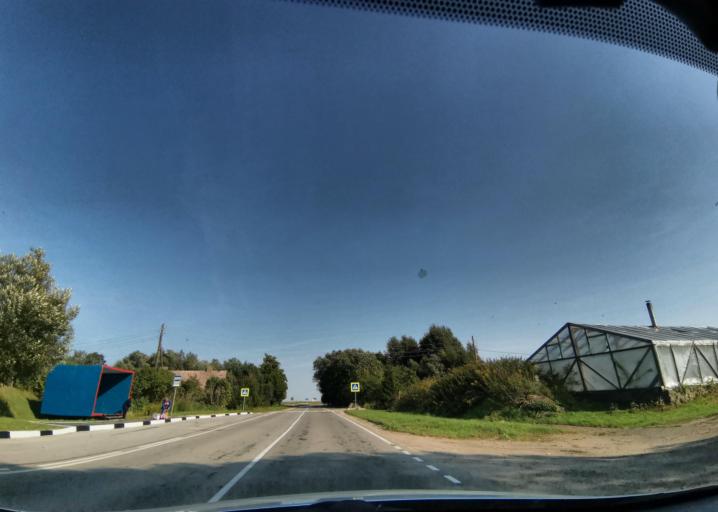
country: RU
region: Kaliningrad
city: Neman
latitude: 55.0173
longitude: 22.1110
